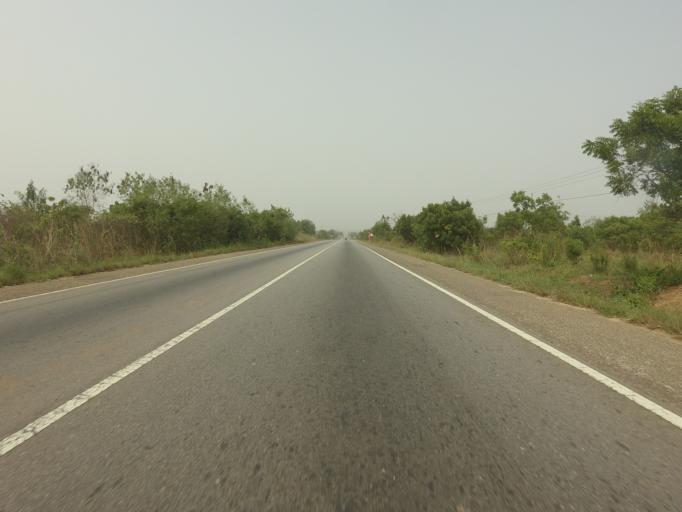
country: GH
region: Volta
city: Anloga
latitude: 5.9491
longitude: 0.5240
